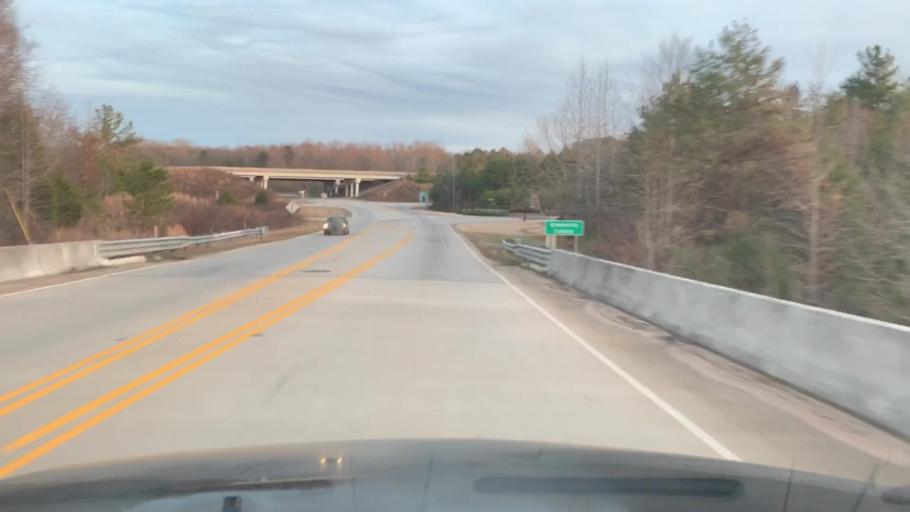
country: US
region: South Carolina
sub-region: Greenville County
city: Golden Grove
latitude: 34.7644
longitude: -82.4543
